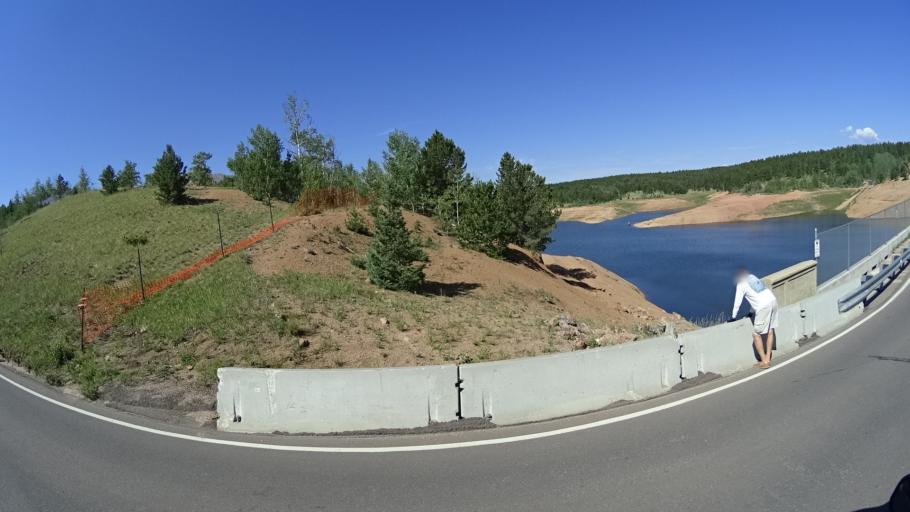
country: US
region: Colorado
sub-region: El Paso County
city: Cascade-Chipita Park
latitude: 38.9191
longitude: -105.0220
